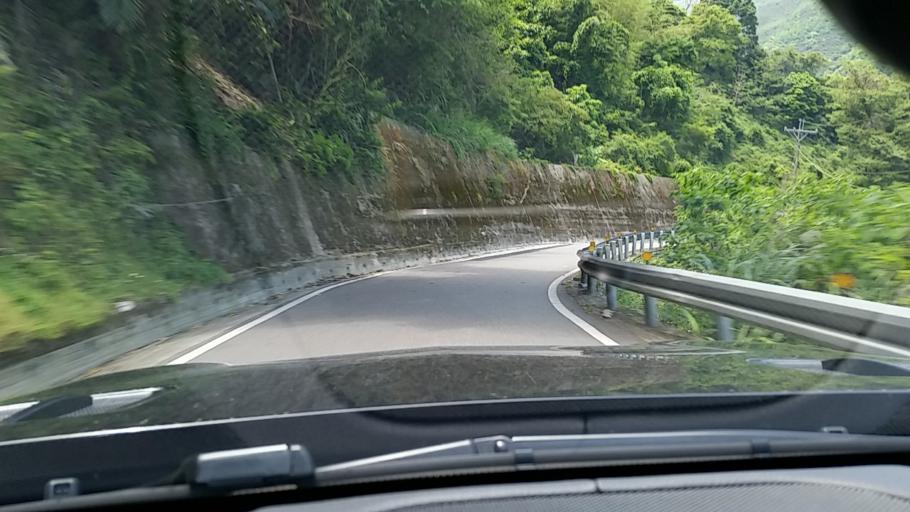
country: TW
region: Taiwan
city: Daxi
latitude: 24.6979
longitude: 121.3669
